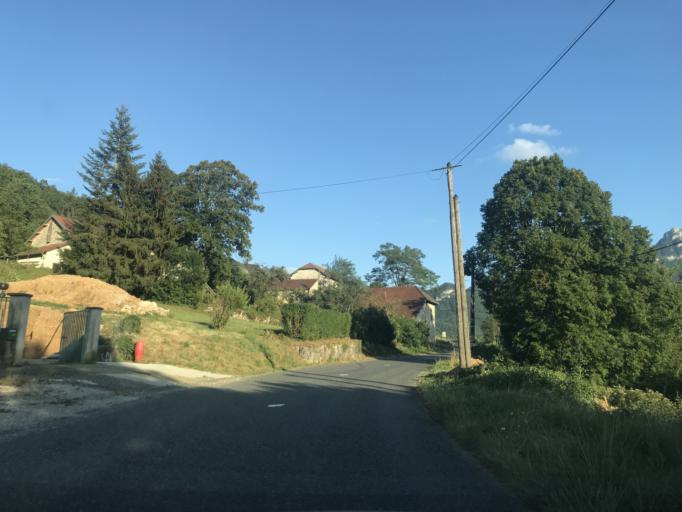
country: FR
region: Rhone-Alpes
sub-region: Departement de la Savoie
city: Yenne
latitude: 45.7172
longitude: 5.8189
